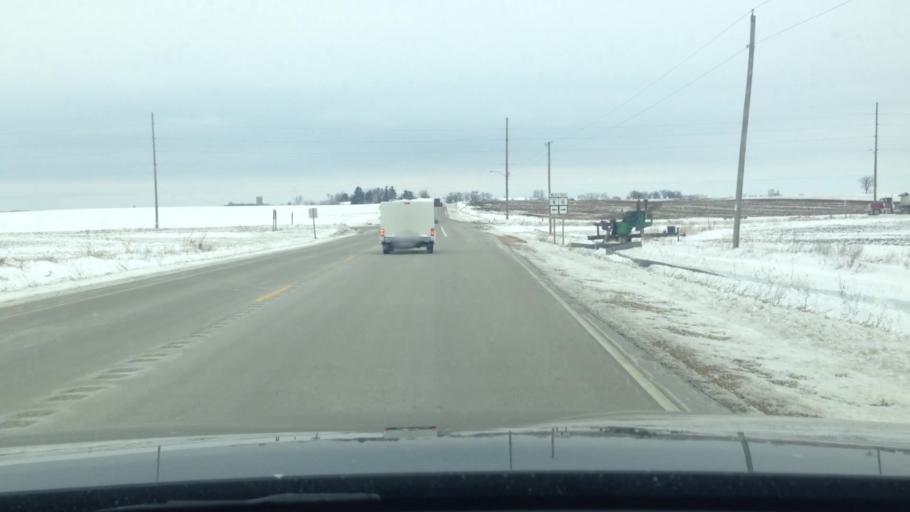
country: US
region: Illinois
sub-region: McHenry County
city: Hebron
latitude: 42.5151
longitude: -88.4427
